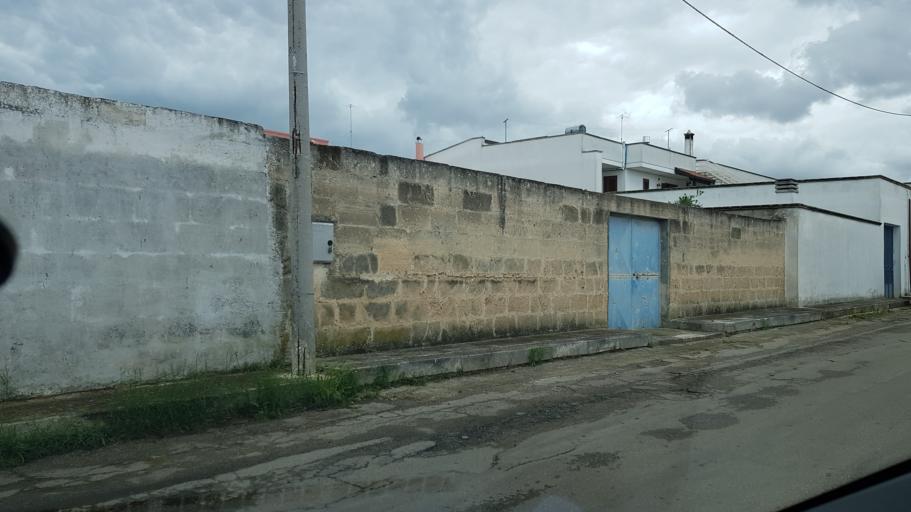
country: IT
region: Apulia
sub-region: Provincia di Brindisi
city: Torchiarolo
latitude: 40.4819
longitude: 18.0498
